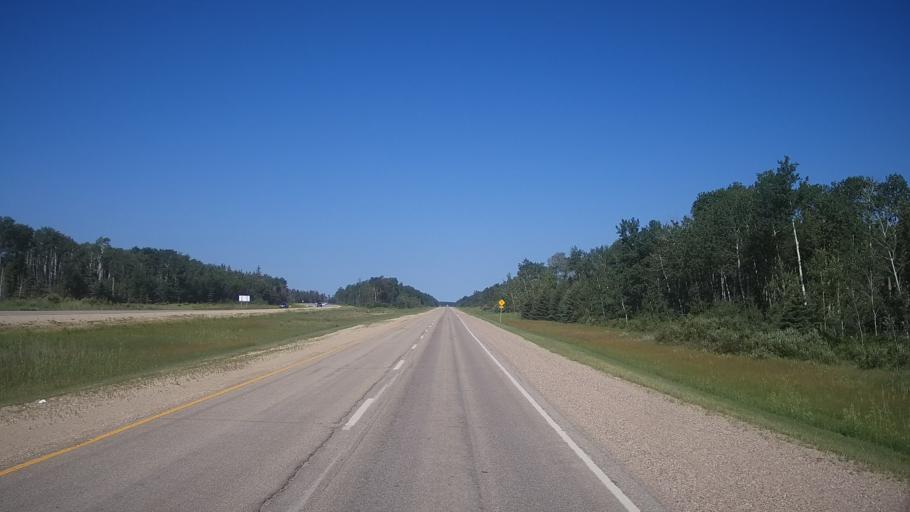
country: CA
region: Manitoba
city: La Broquerie
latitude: 49.6496
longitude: -95.9337
